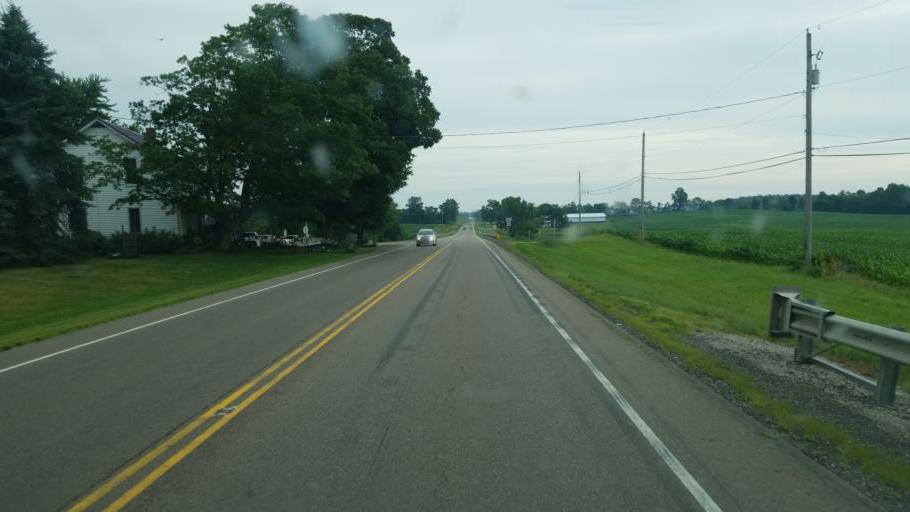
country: US
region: Ohio
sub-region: Knox County
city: Fredericktown
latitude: 40.5227
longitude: -82.5480
